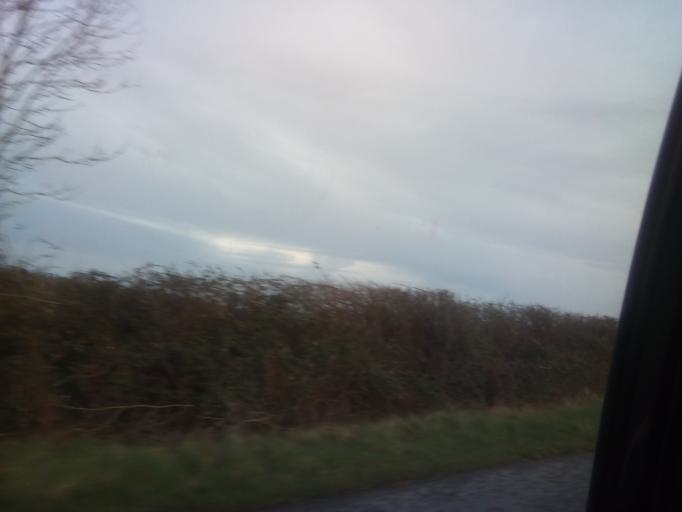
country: IE
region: Leinster
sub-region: Laois
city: Abbeyleix
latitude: 52.8551
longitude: -7.3864
